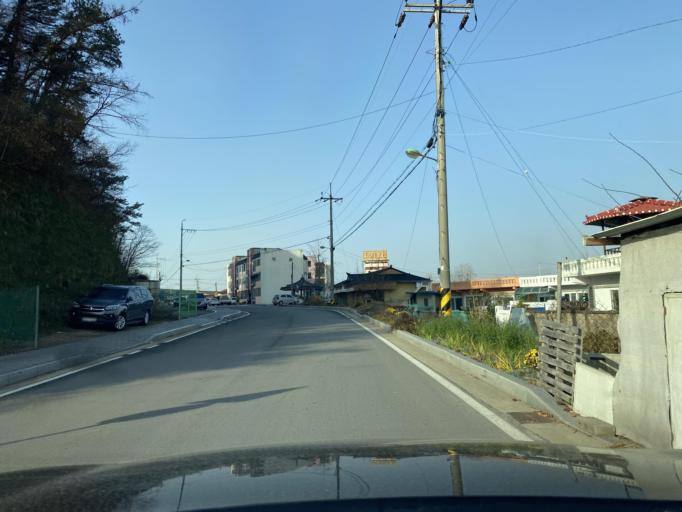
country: KR
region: Chungcheongnam-do
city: Yesan
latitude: 36.6796
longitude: 126.8312
